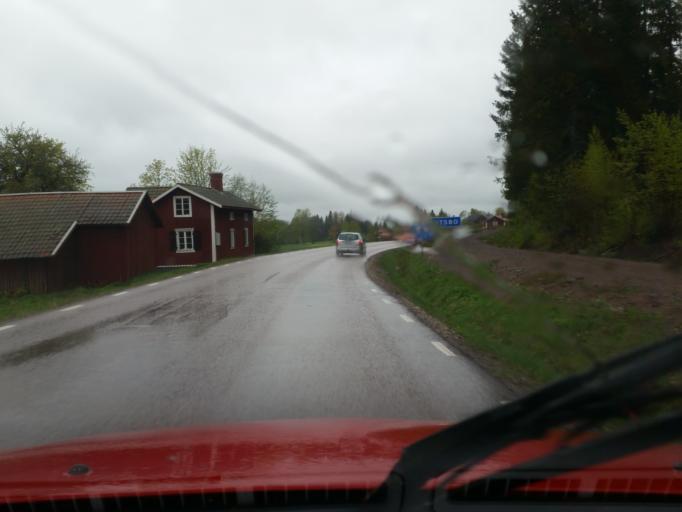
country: SE
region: Dalarna
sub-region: Saters Kommun
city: Saeter
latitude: 60.3481
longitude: 15.7815
